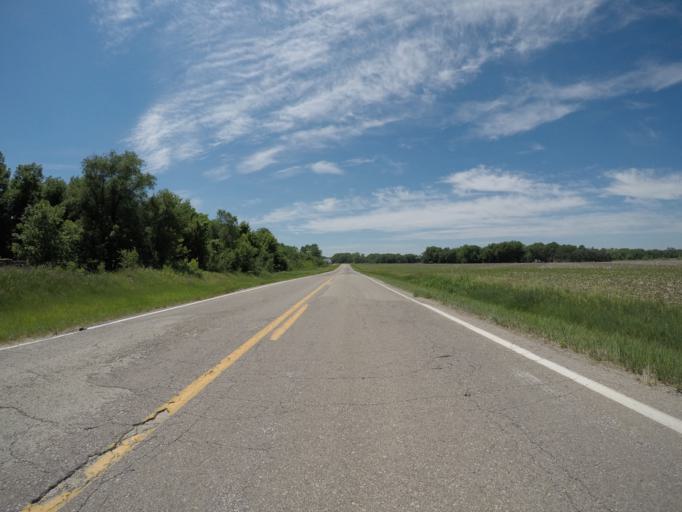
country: US
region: Kansas
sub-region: Wabaunsee County
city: Alma
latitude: 39.0393
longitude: -96.2655
